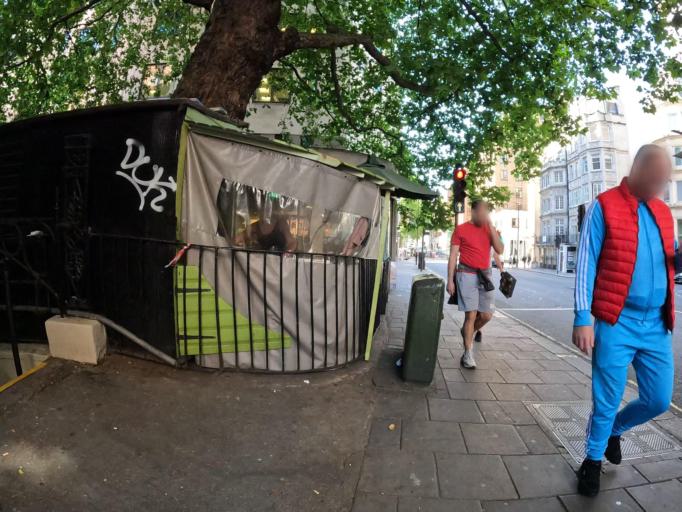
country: GB
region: England
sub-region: Greater London
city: London
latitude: 51.5087
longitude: -0.1438
